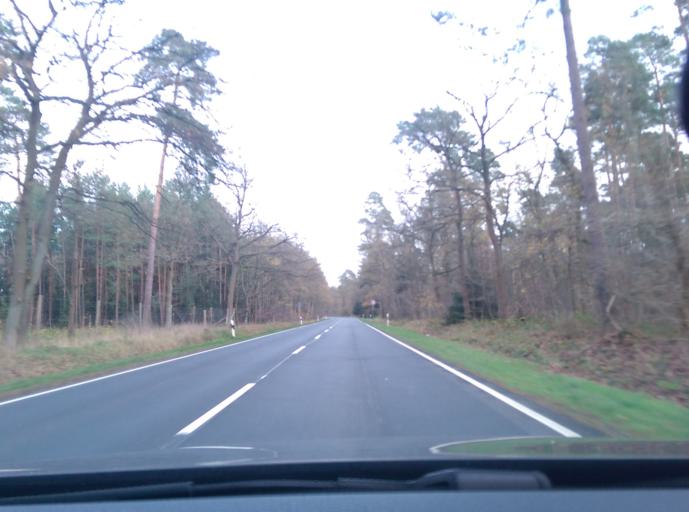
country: DE
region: Lower Saxony
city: Hambuhren
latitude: 52.5932
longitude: 9.9615
